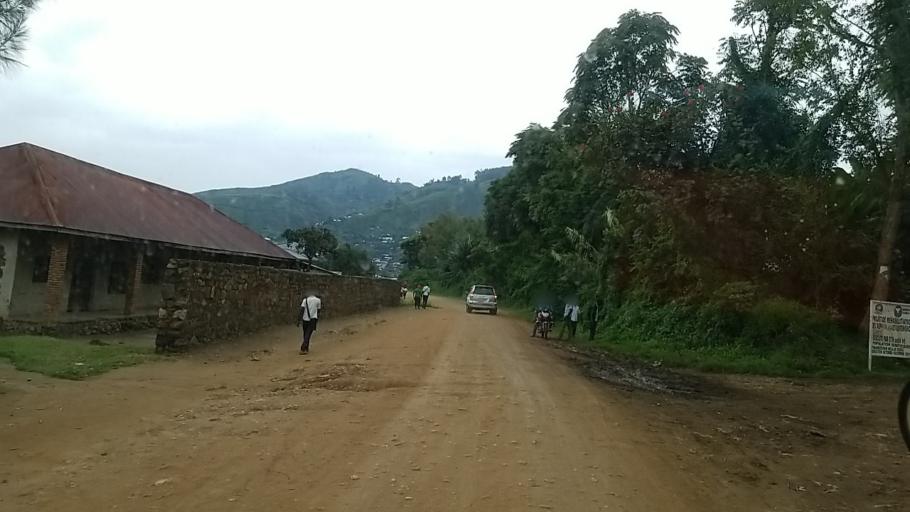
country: CD
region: Nord Kivu
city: Sake
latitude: -1.7033
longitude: 29.0169
